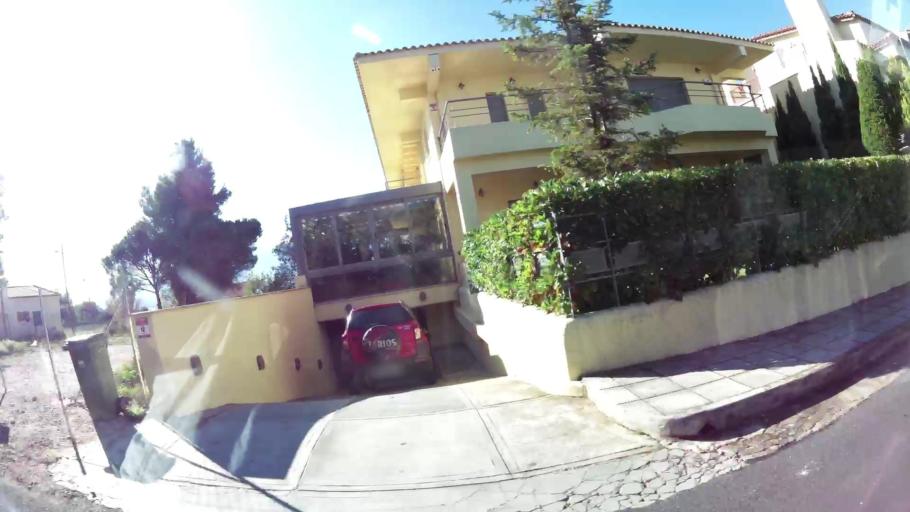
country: GR
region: Attica
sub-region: Nomarchia Anatolikis Attikis
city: Anoixi
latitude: 38.1333
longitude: 23.8661
